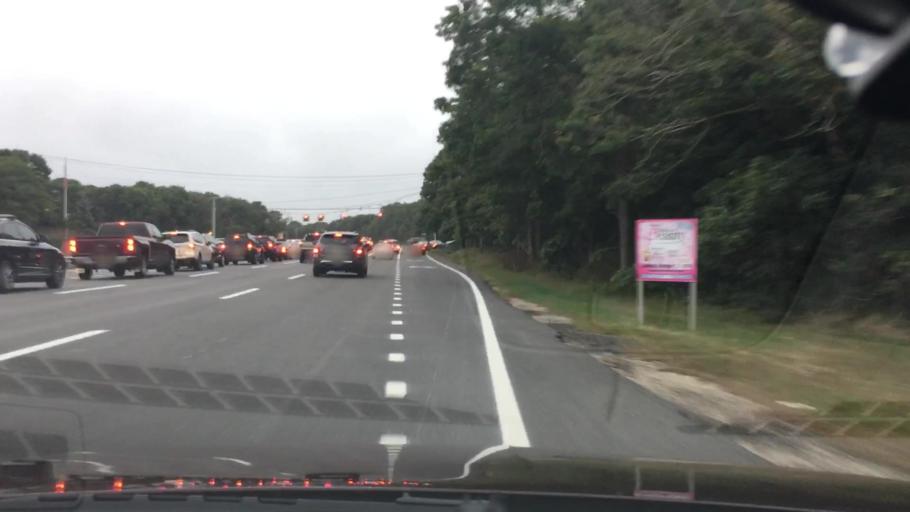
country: US
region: New York
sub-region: Suffolk County
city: Centereach
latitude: 40.8843
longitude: -73.1079
